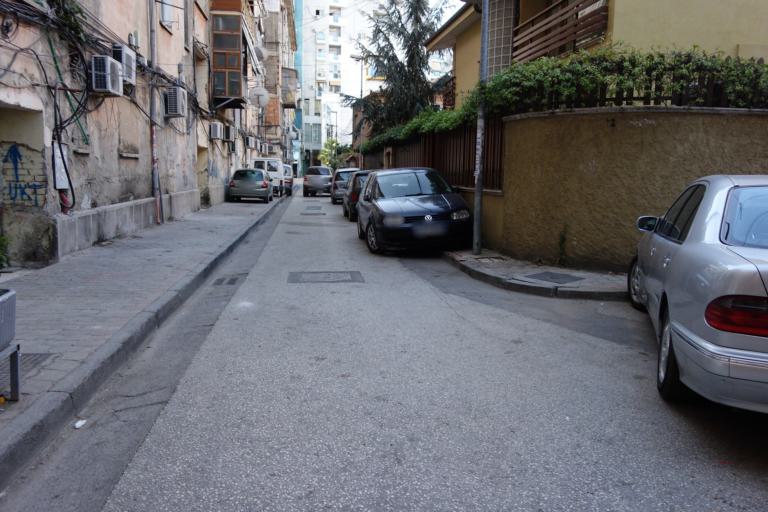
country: AL
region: Tirane
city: Tirana
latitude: 41.3246
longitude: 19.8124
